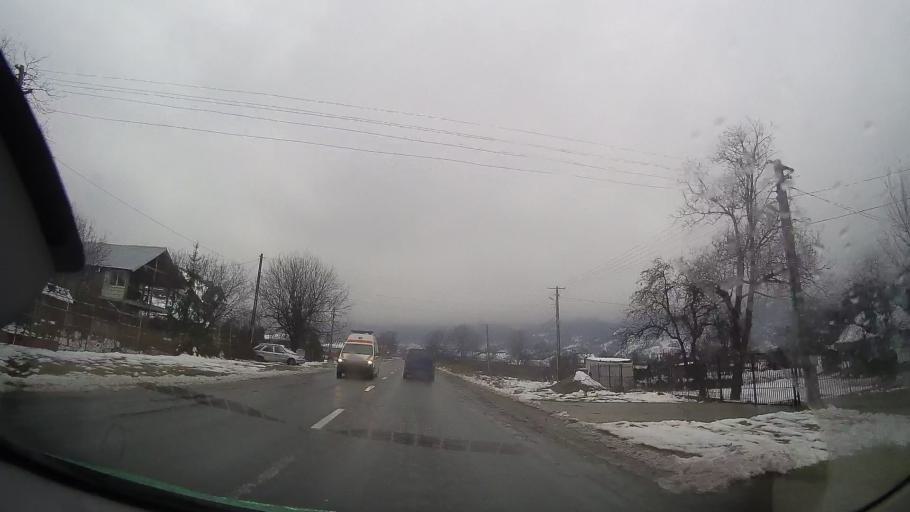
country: RO
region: Neamt
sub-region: Comuna Pangarati
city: Stejaru
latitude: 46.9150
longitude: 26.1857
